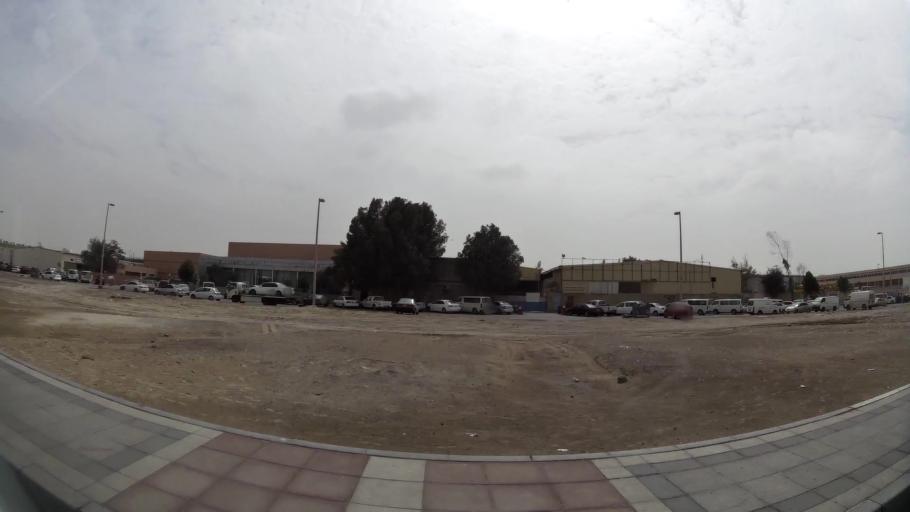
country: AE
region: Abu Dhabi
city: Abu Dhabi
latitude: 24.3556
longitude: 54.5198
